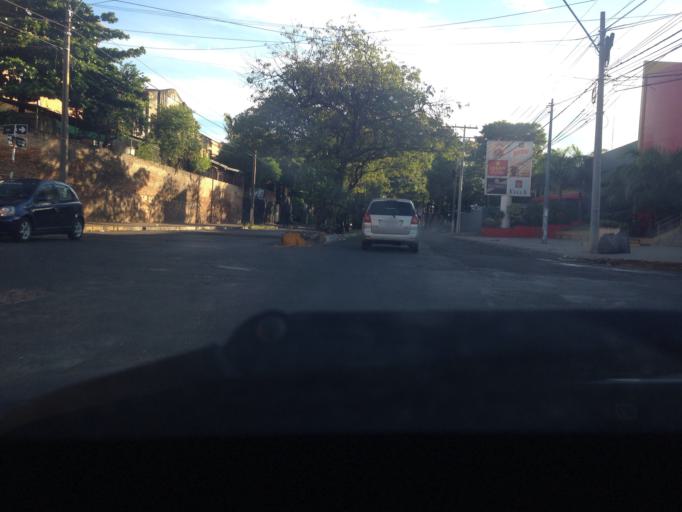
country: PY
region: Central
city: Lambare
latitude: -25.3144
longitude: -57.5888
